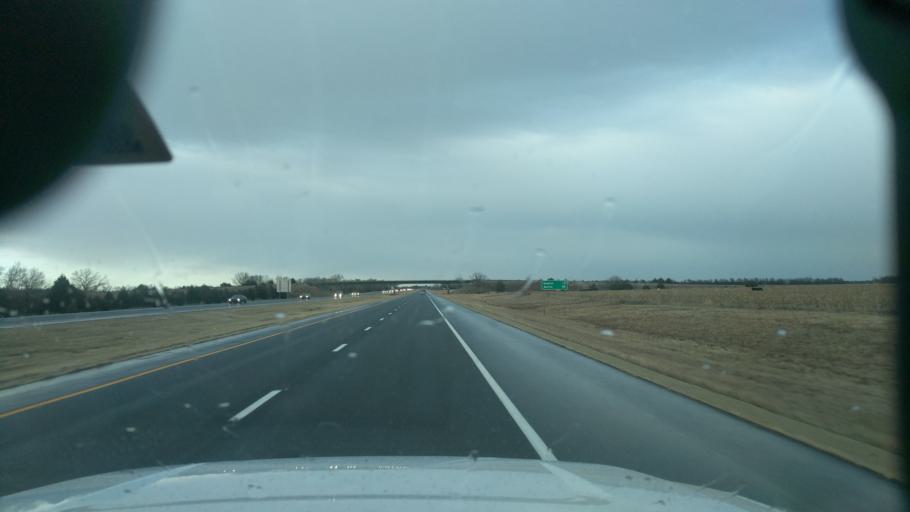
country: US
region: Kansas
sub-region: Harvey County
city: Newton
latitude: 37.9668
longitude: -97.3271
